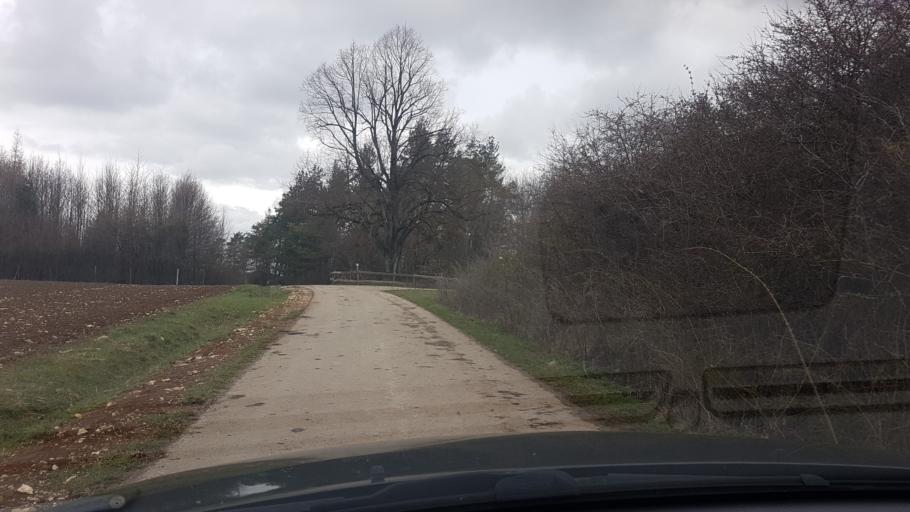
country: DE
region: Bavaria
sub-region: Upper Franconia
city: Heiligenstadt
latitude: 49.8636
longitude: 11.0949
